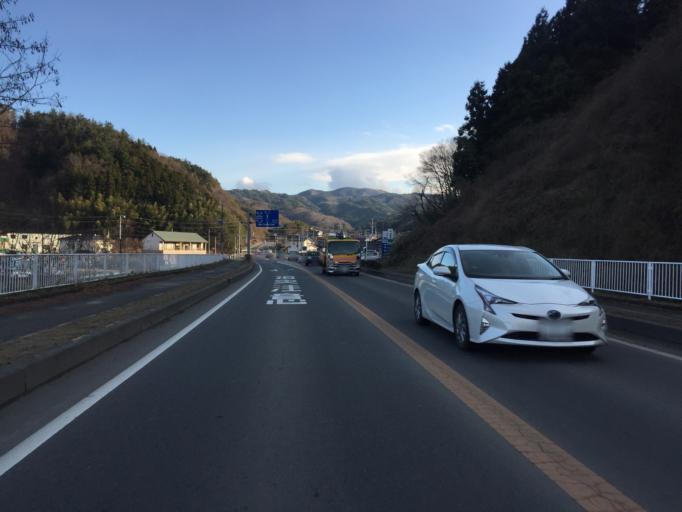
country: JP
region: Fukushima
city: Fukushima-shi
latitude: 37.6577
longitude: 140.6057
